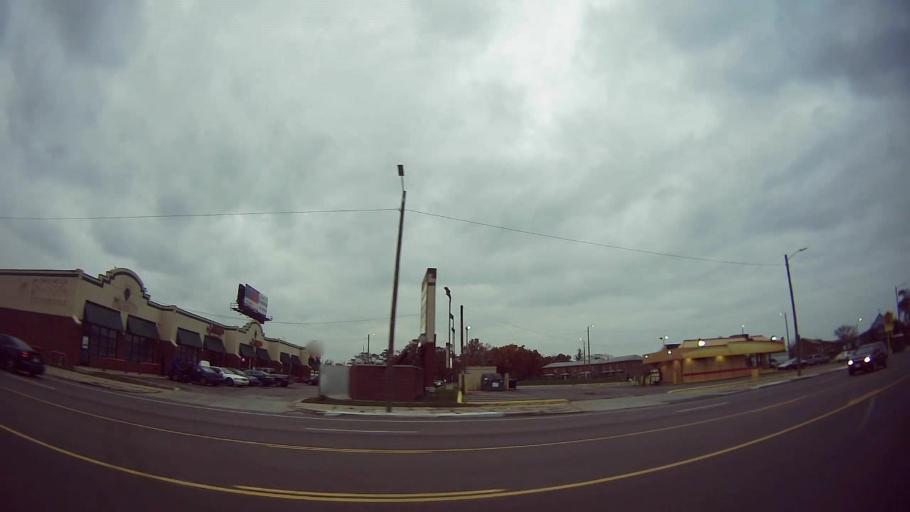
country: US
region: Michigan
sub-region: Wayne County
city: Grosse Pointe Park
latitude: 42.3890
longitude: -82.9780
